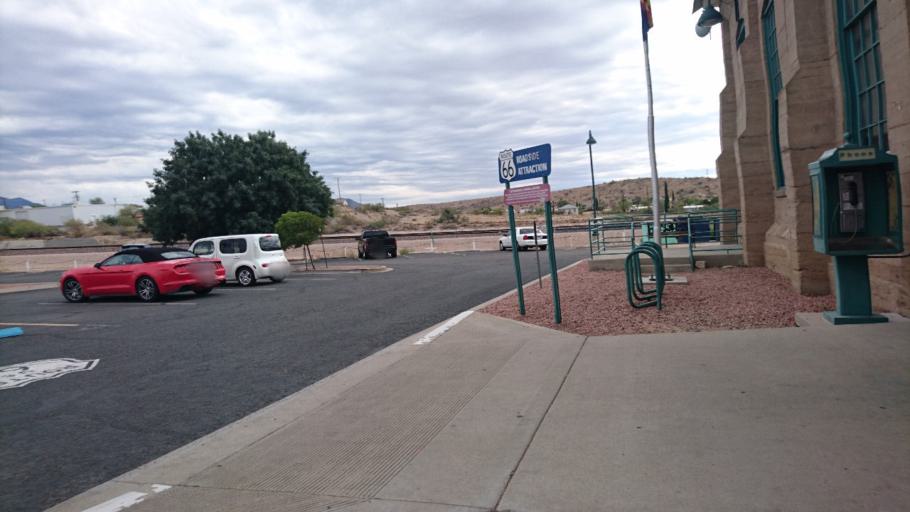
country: US
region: Arizona
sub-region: Mohave County
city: Kingman
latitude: 35.1891
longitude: -114.0586
